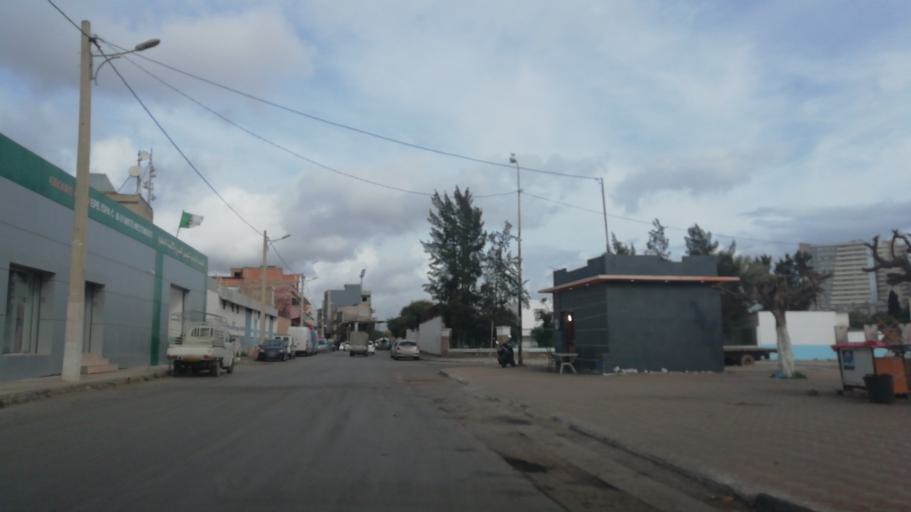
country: DZ
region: Oran
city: Oran
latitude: 35.6824
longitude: -0.6411
